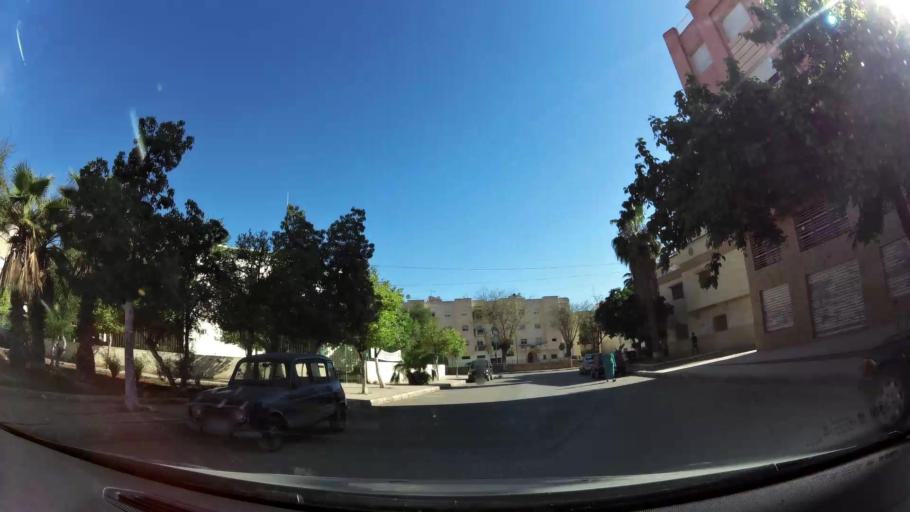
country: MA
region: Meknes-Tafilalet
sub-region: Meknes
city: Meknes
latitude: 33.8924
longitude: -5.5009
